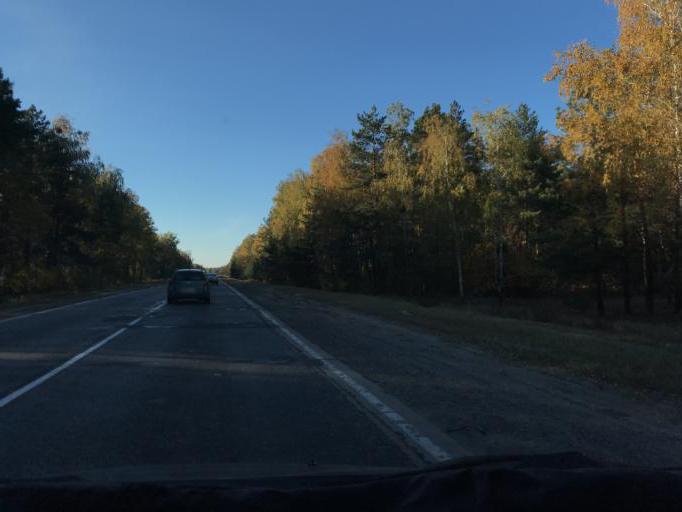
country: BY
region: Gomel
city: Mazyr
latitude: 52.2332
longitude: 28.9574
